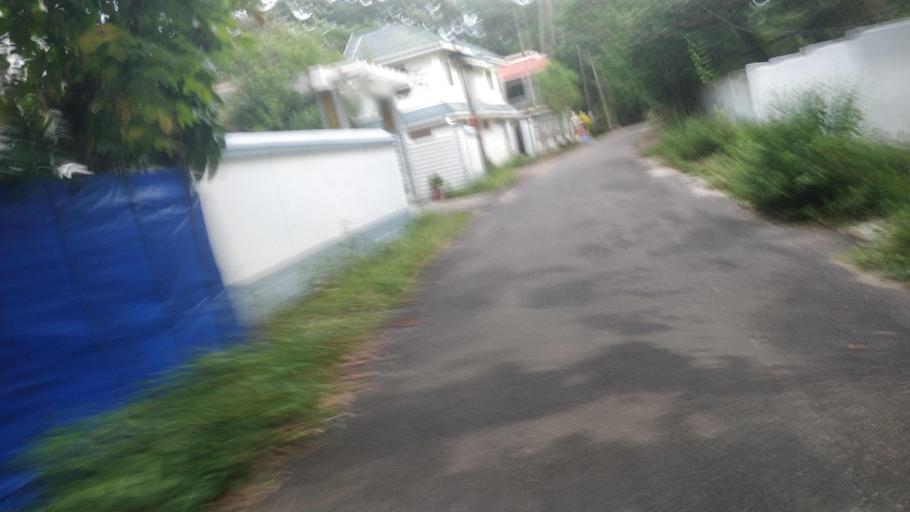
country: IN
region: Kerala
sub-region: Alappuzha
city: Vayalar
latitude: 9.7091
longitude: 76.3494
